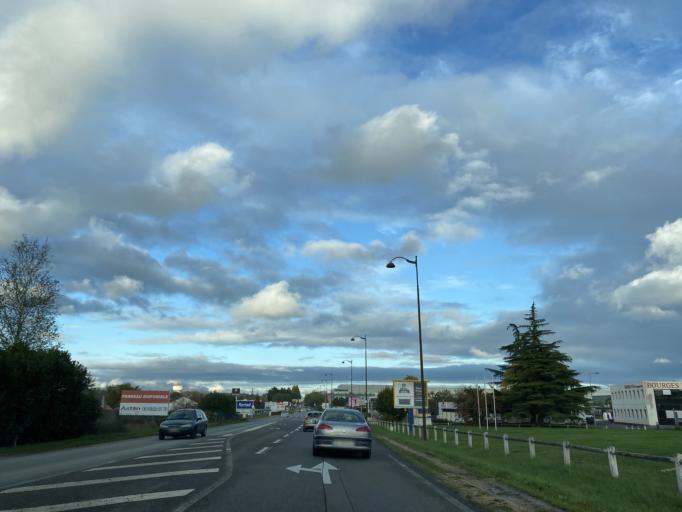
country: FR
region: Centre
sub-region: Departement du Cher
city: Bourges
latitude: 47.0632
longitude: 2.3670
